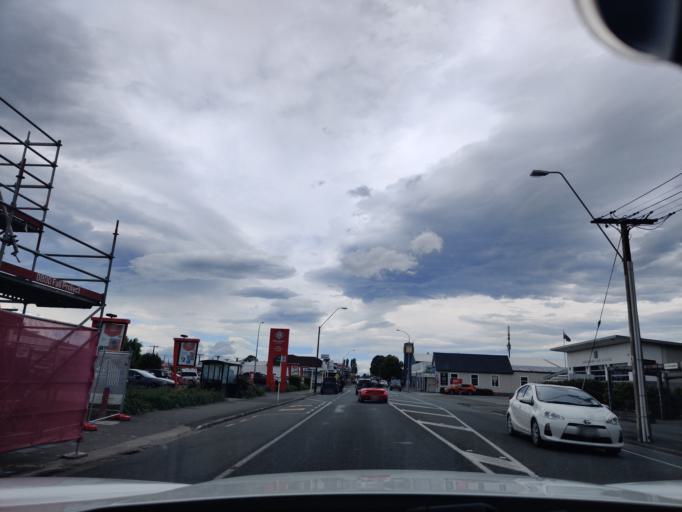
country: NZ
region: Wellington
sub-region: Masterton District
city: Masterton
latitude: -41.0264
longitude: 175.5261
